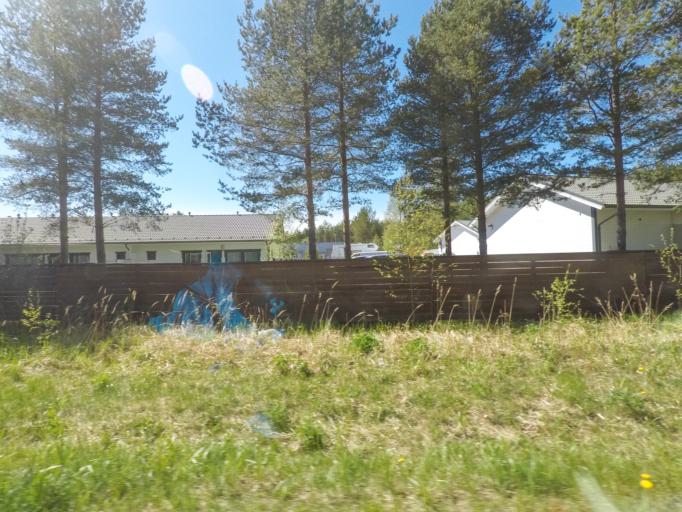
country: FI
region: Uusimaa
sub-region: Helsinki
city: Sammatti
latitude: 60.3274
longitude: 23.8132
